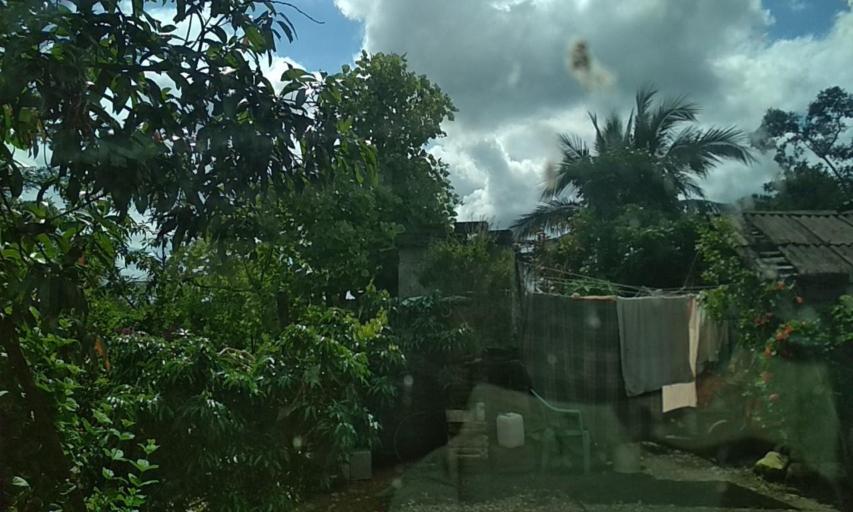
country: MX
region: Veracruz
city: Gutierrez Zamora
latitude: 20.2856
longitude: -97.1284
